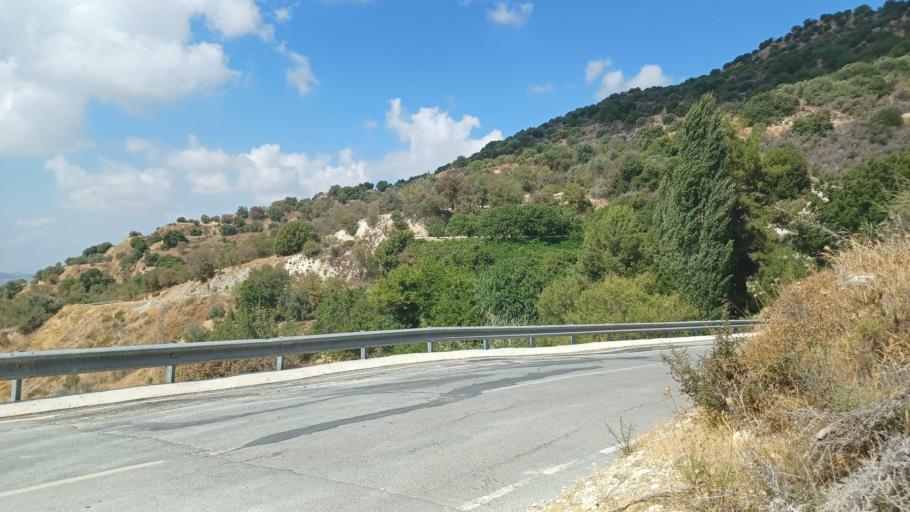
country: CY
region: Limassol
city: Pachna
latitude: 34.8025
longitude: 32.6746
